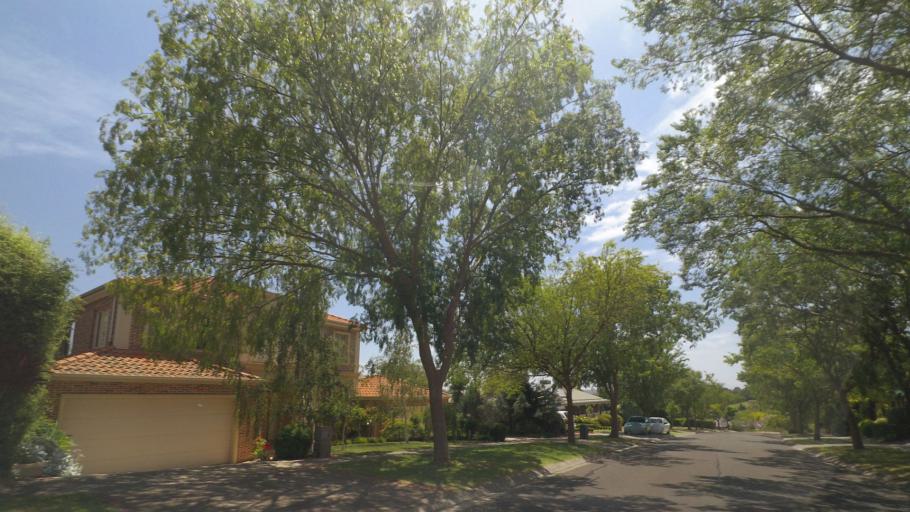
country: AU
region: Victoria
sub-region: Yarra Ranges
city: Chirnside Park
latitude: -37.7598
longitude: 145.3057
